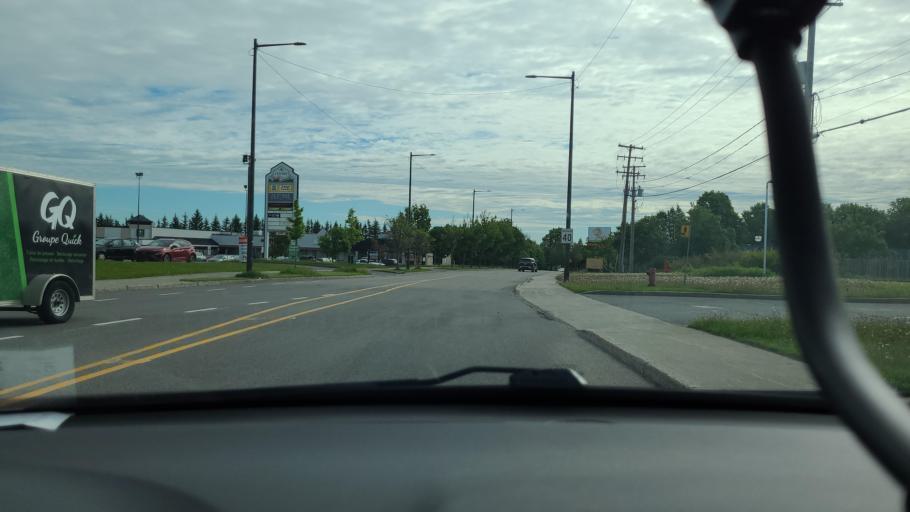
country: CA
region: Quebec
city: L'Ancienne-Lorette
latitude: 46.7649
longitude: -71.3705
